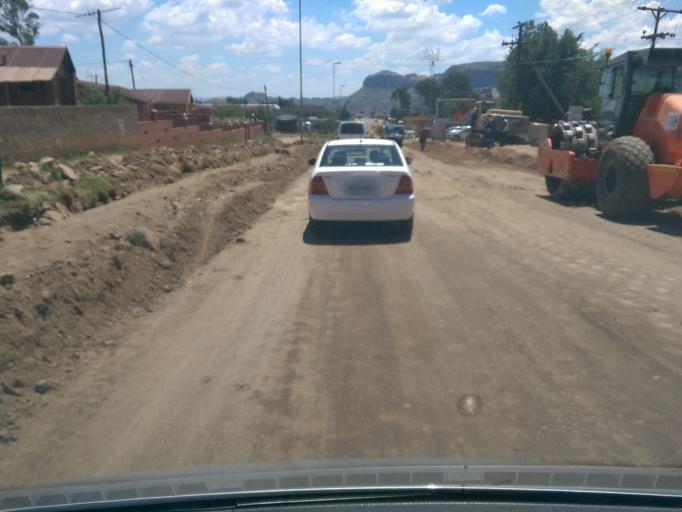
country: LS
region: Maseru
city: Nako
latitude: -29.4500
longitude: 27.7185
